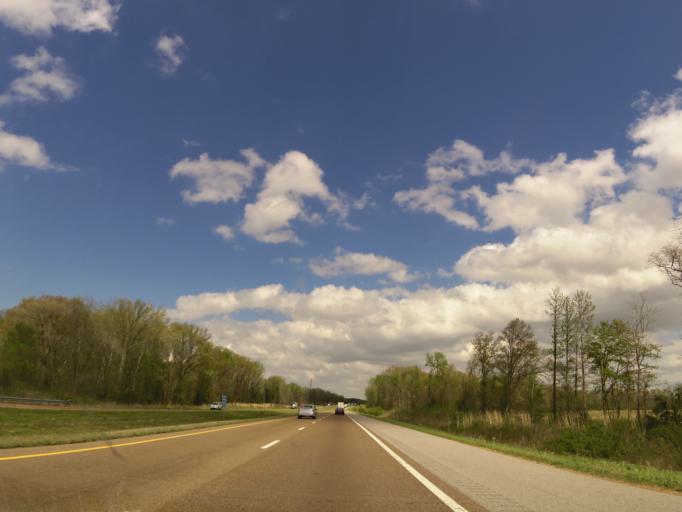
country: US
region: Tennessee
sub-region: Fayette County
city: Hickory Withe
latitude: 35.3266
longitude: -89.5620
